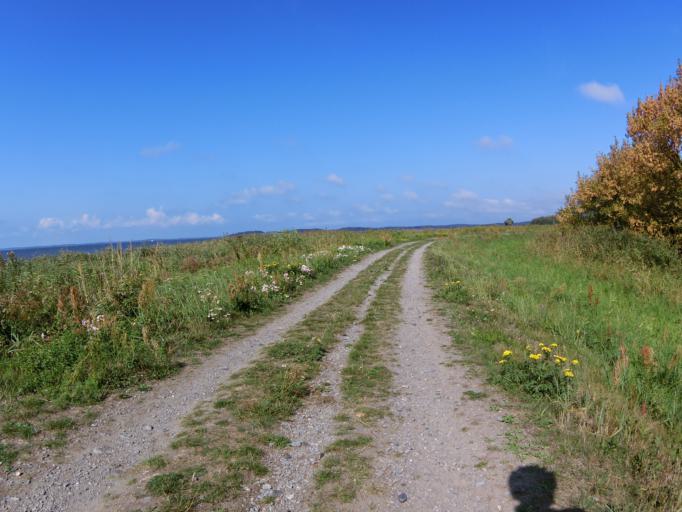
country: DE
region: Mecklenburg-Vorpommern
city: Loddin
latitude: 53.9927
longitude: 14.0473
